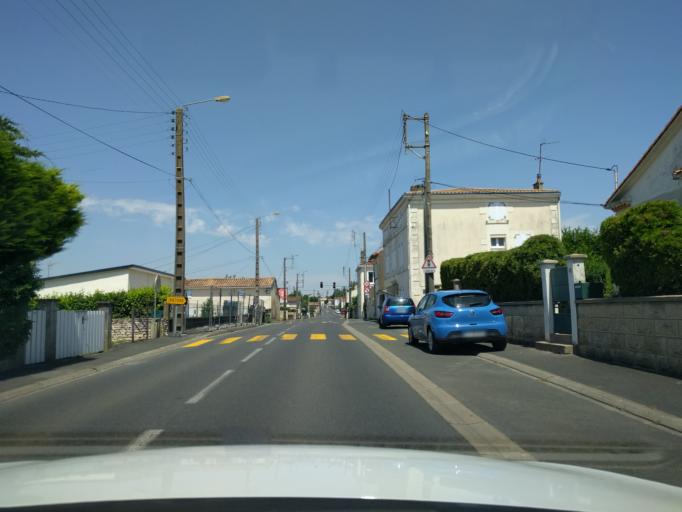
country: FR
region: Poitou-Charentes
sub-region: Departement des Deux-Sevres
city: Niort
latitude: 46.3470
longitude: -0.4771
